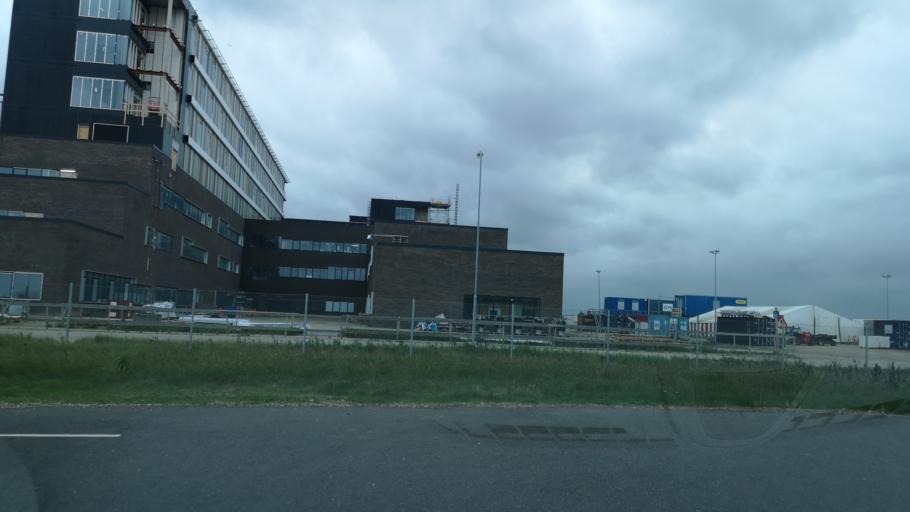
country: DK
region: Central Jutland
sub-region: Herning Kommune
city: Snejbjerg
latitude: 56.1591
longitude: 8.8897
